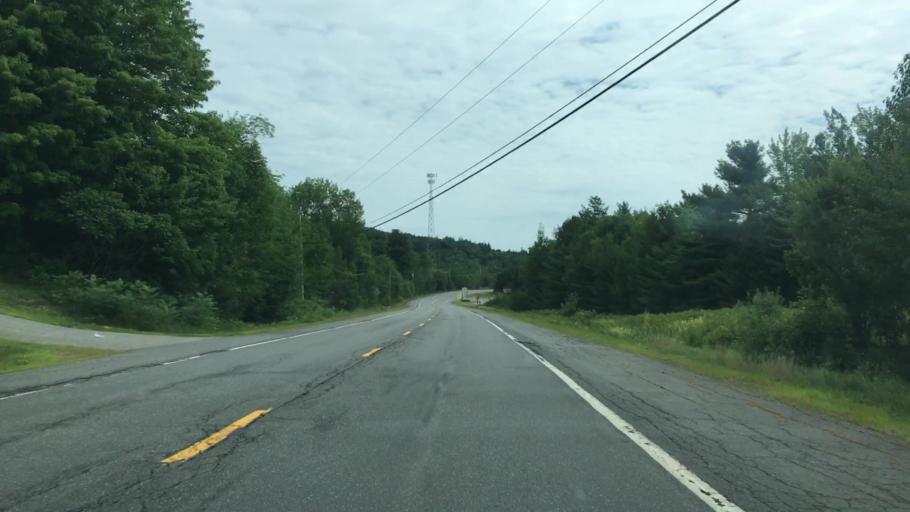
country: US
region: Maine
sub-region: Washington County
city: Calais
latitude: 45.1148
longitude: -67.4068
